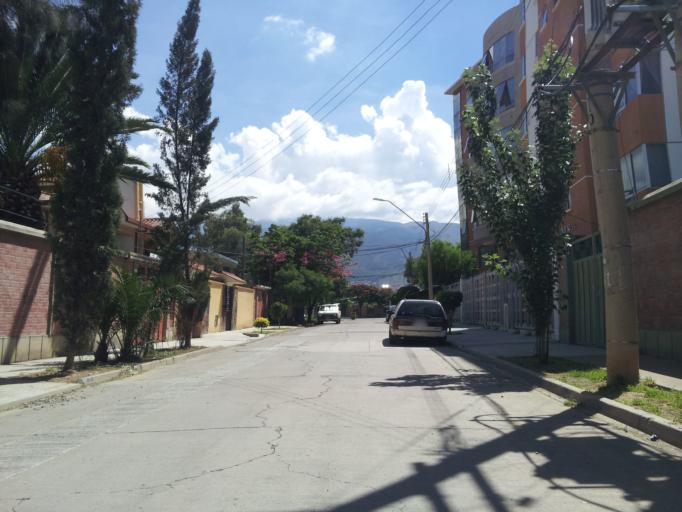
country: BO
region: Cochabamba
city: Cochabamba
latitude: -17.3838
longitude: -66.1722
